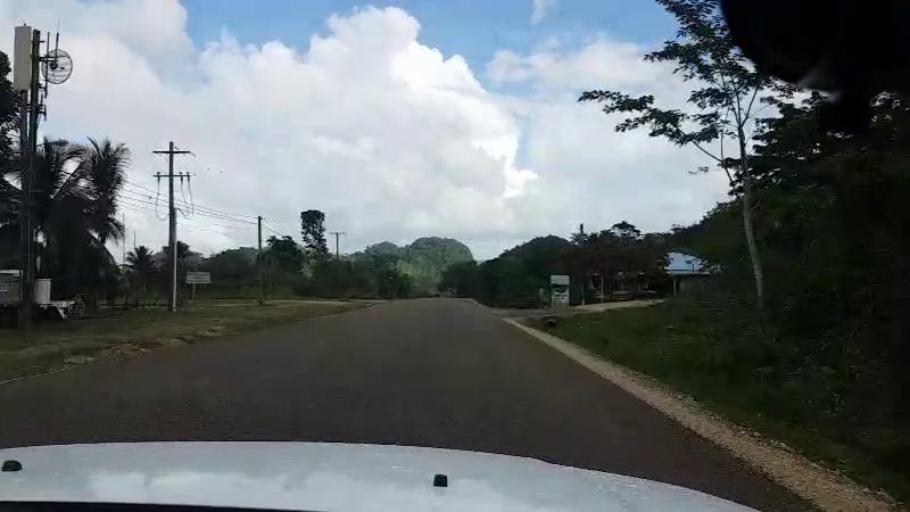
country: BZ
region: Cayo
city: Belmopan
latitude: 17.0916
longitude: -88.6355
